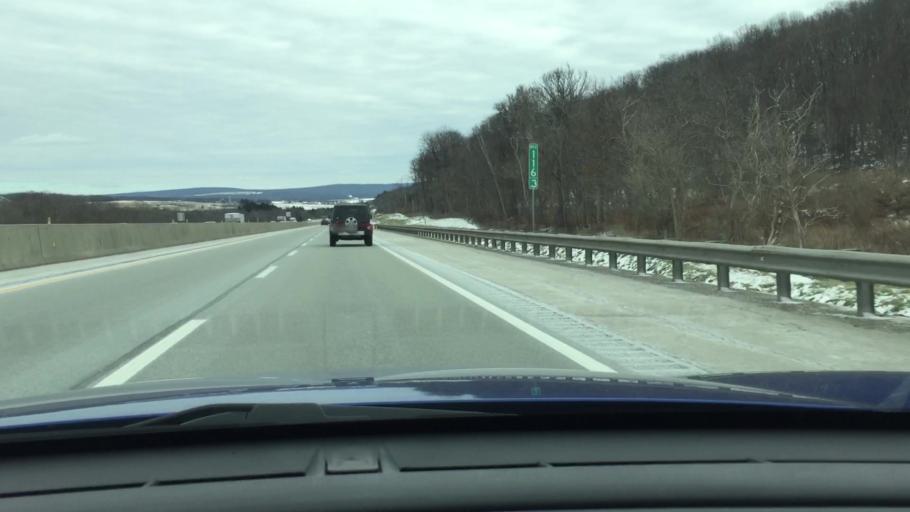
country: US
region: Pennsylvania
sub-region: Somerset County
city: Friedens
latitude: 39.9876
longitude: -78.9741
